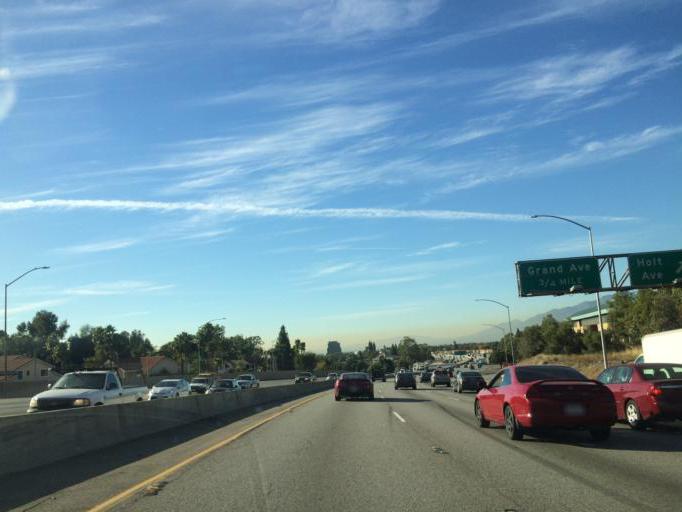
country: US
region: California
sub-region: Los Angeles County
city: Covina
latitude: 34.0684
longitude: -117.8601
